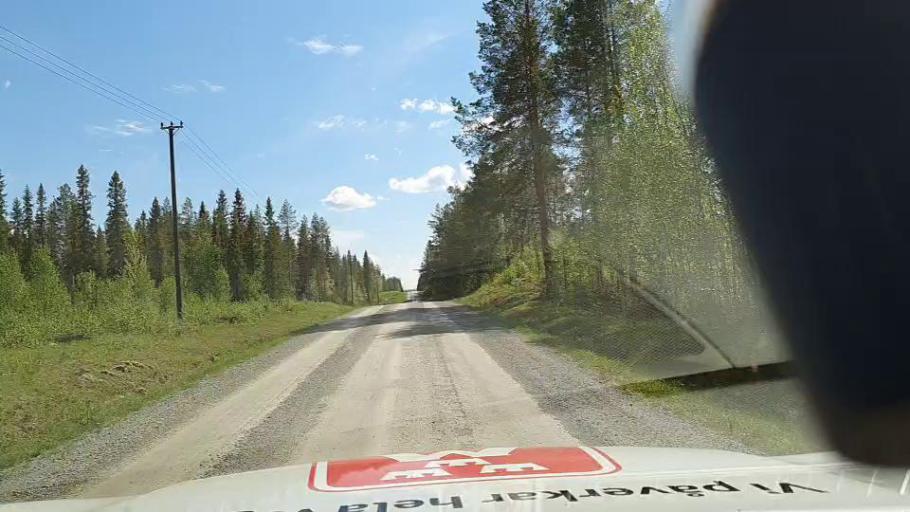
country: SE
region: Jaemtland
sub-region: Stroemsunds Kommun
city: Stroemsund
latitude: 64.4813
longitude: 15.5923
